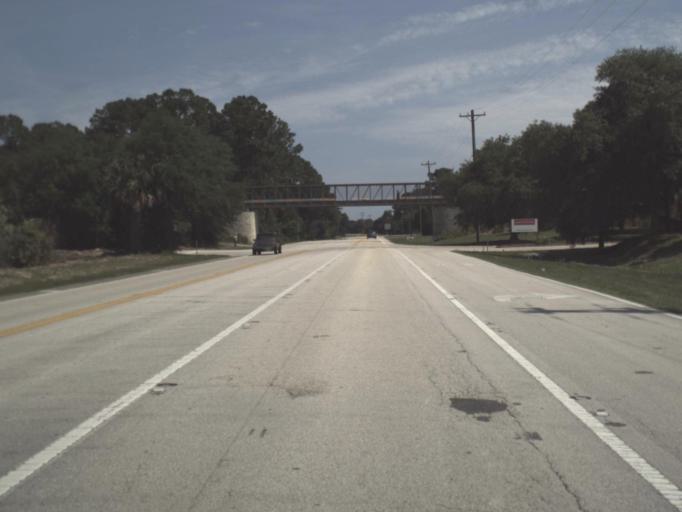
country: US
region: Florida
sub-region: Duval County
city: Atlantic Beach
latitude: 30.3911
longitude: -81.4575
